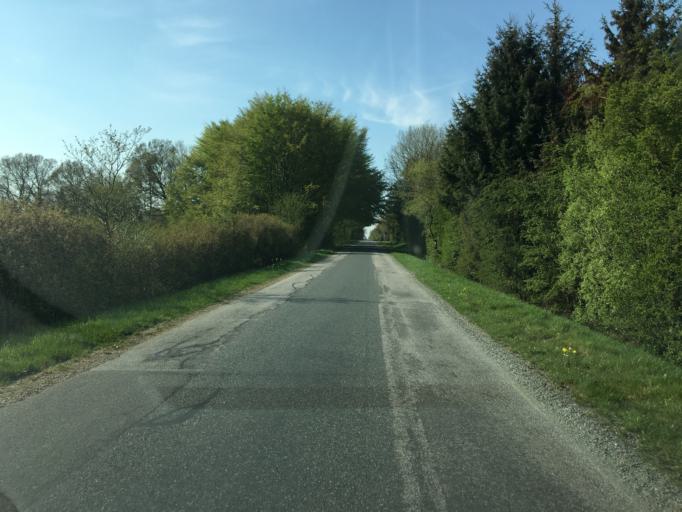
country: DK
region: South Denmark
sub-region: Haderslev Kommune
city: Vojens
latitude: 55.2391
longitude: 9.3235
